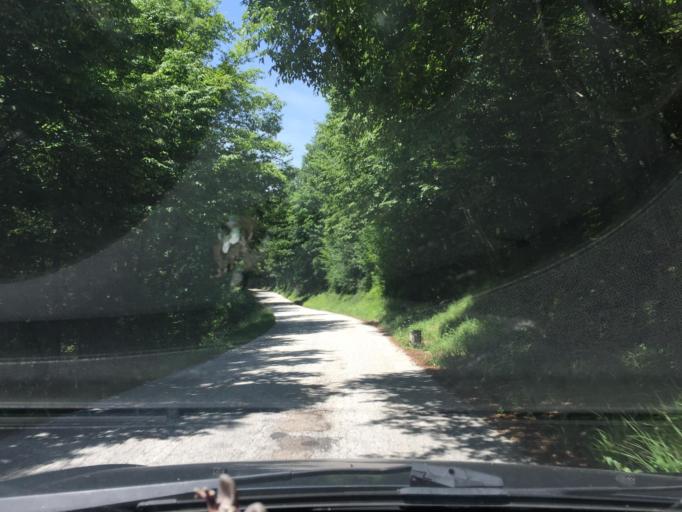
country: HR
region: Istarska
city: Buzet
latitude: 45.4724
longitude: 14.1030
